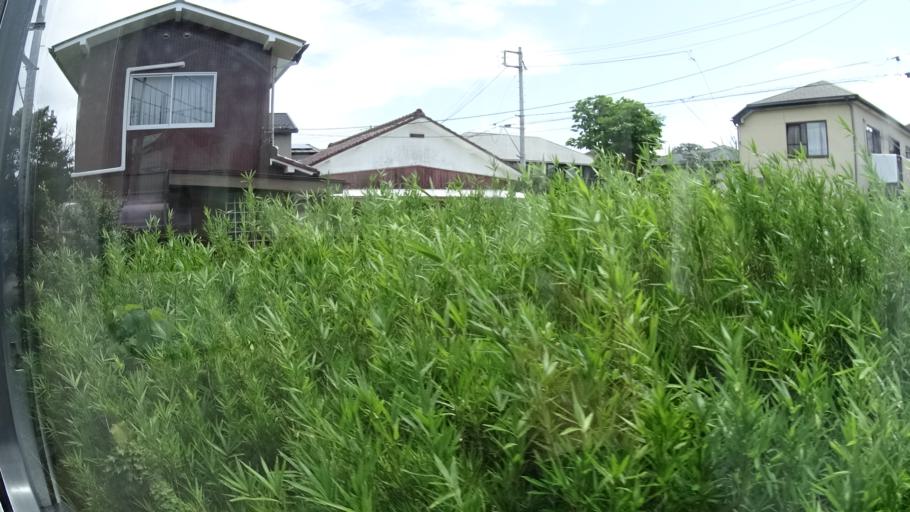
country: JP
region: Kanagawa
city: Fujisawa
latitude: 35.3171
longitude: 139.4819
